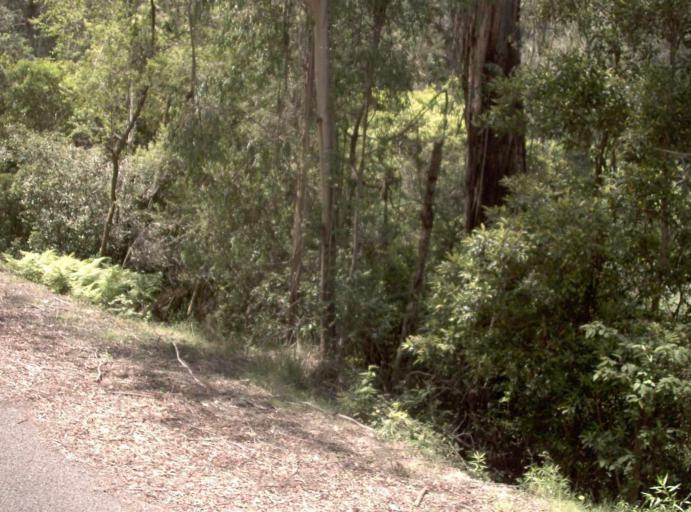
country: AU
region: New South Wales
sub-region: Bombala
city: Bombala
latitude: -37.4428
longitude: 148.9473
